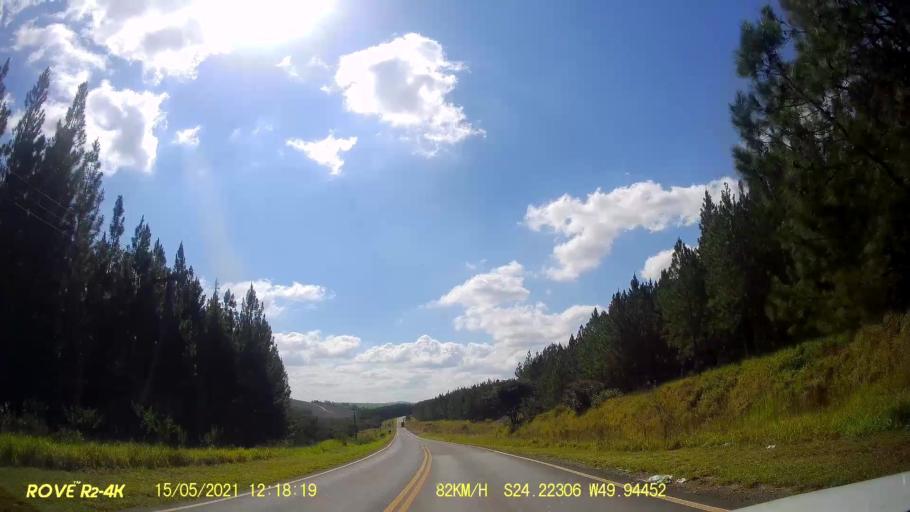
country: BR
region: Parana
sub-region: Jaguariaiva
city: Jaguariaiva
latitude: -24.2231
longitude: -49.9447
